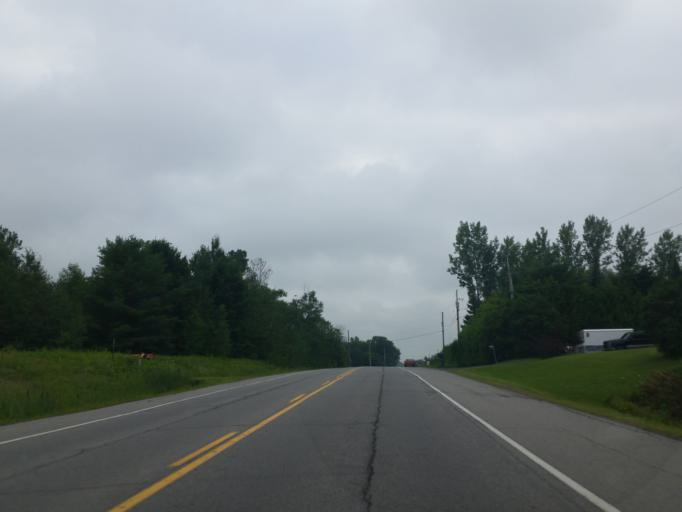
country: CA
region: Ontario
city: Clarence-Rockland
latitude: 45.3789
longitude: -75.3835
